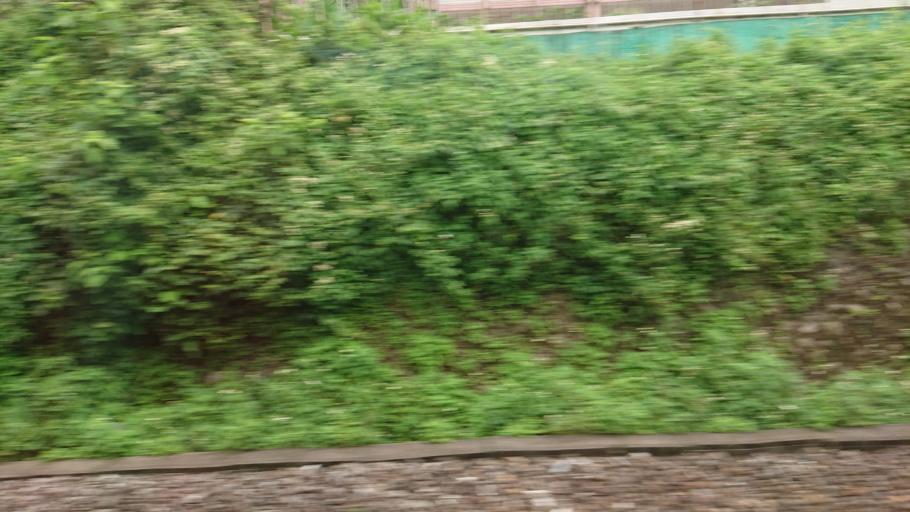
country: TW
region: Taiwan
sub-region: Yilan
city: Yilan
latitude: 24.9356
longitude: 121.8858
